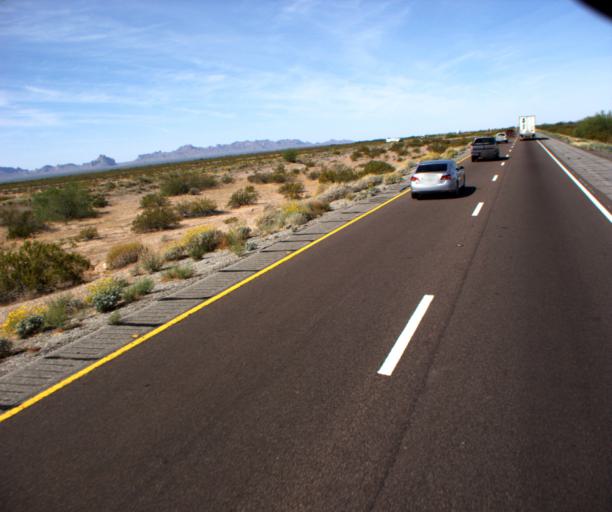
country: US
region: Arizona
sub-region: La Paz County
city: Salome
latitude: 33.5433
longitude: -113.1823
